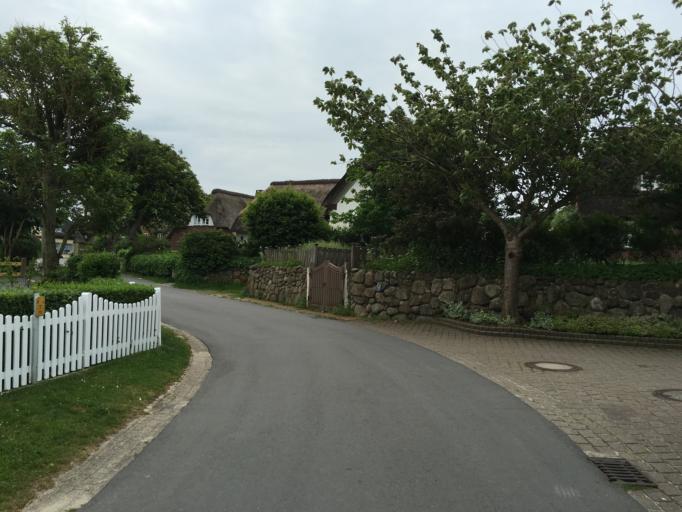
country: DE
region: Schleswig-Holstein
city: Norddorf
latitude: 54.6805
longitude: 8.3362
